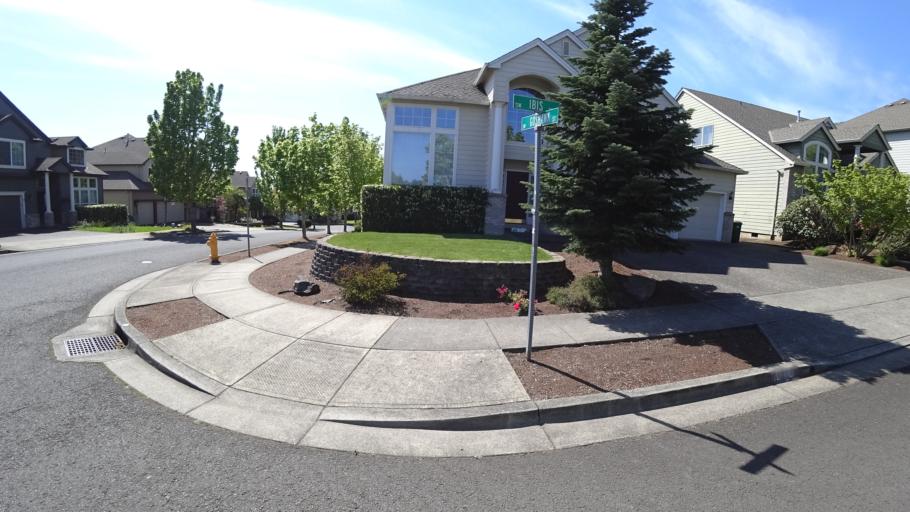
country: US
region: Oregon
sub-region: Washington County
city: King City
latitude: 45.4321
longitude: -122.8442
